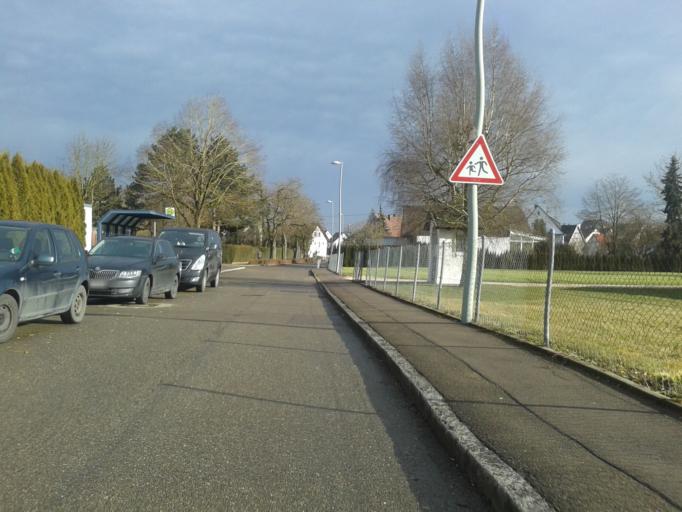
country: DE
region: Baden-Wuerttemberg
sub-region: Tuebingen Region
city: Erbach
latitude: 48.3540
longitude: 9.8982
